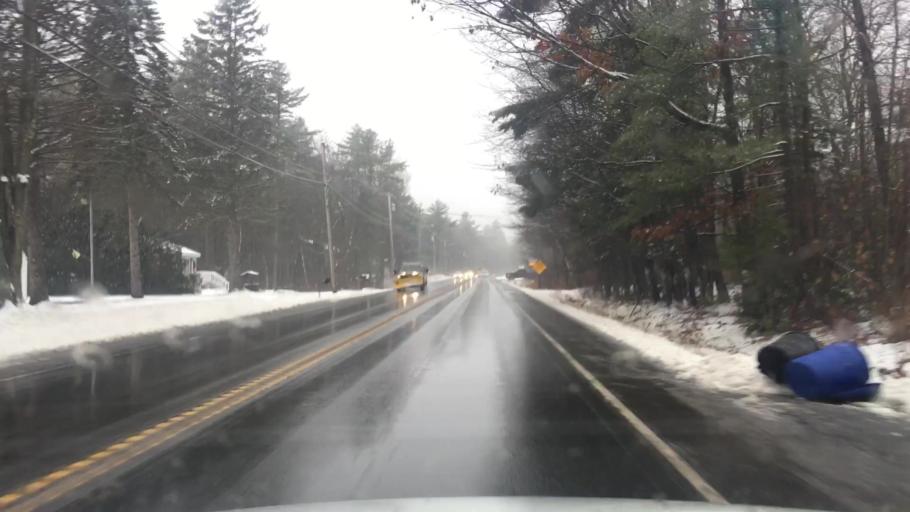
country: US
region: Maine
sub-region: York County
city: Buxton
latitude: 43.7129
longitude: -70.5164
